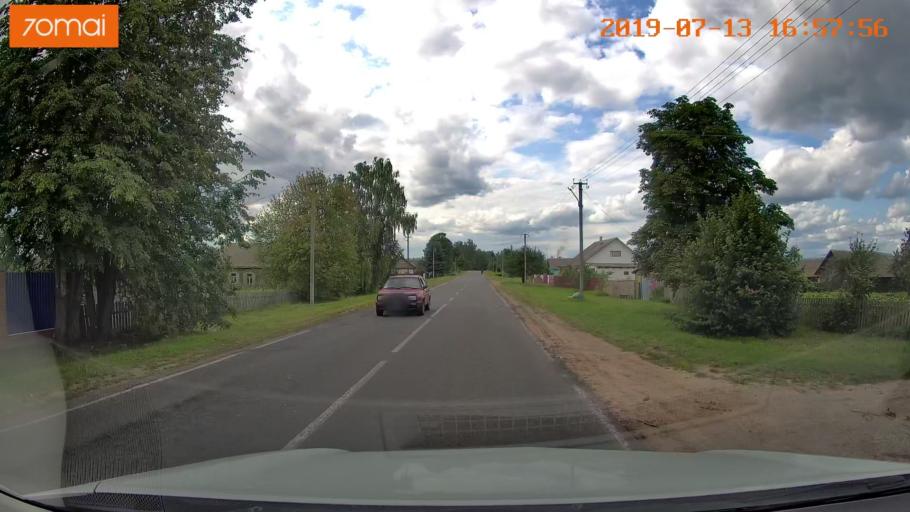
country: BY
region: Mogilev
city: Kirawsk
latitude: 53.2840
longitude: 29.4468
